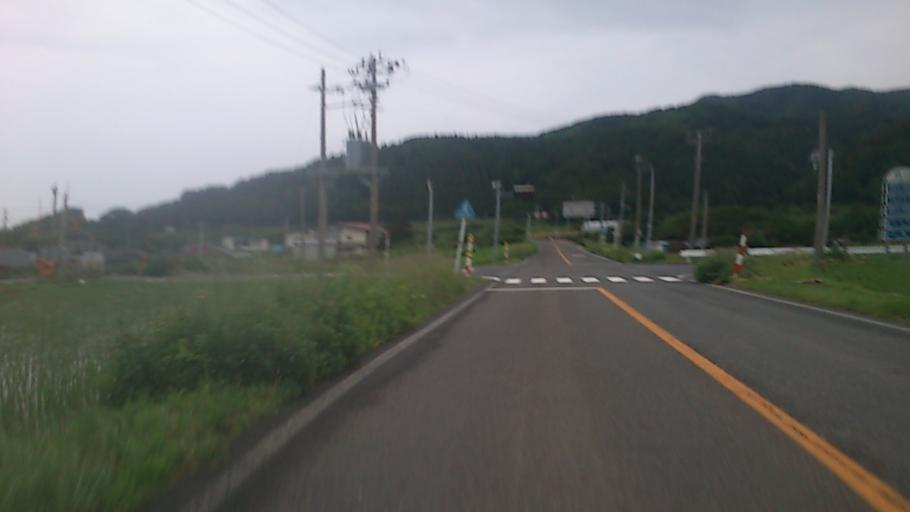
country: JP
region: Akita
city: Noshiromachi
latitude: 40.3755
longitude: 140.0154
